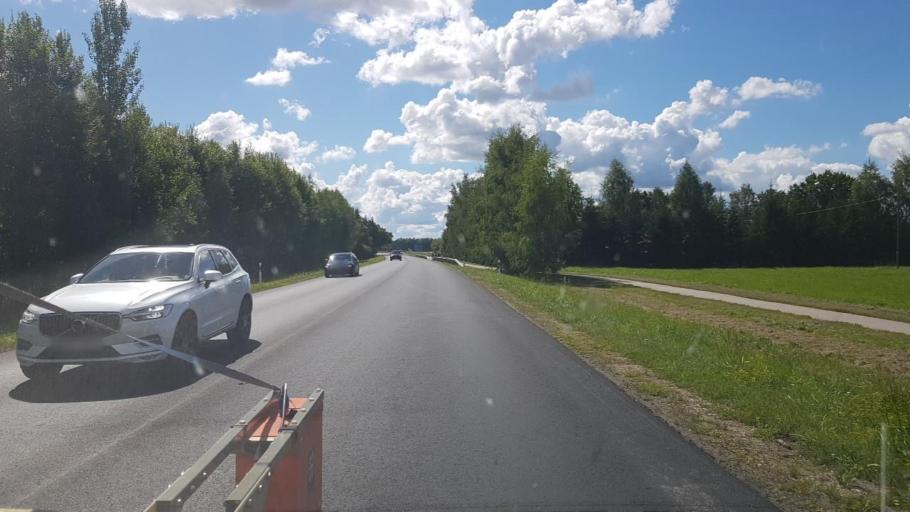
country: EE
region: Viljandimaa
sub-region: Viiratsi vald
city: Viiratsi
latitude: 58.3872
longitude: 25.6779
